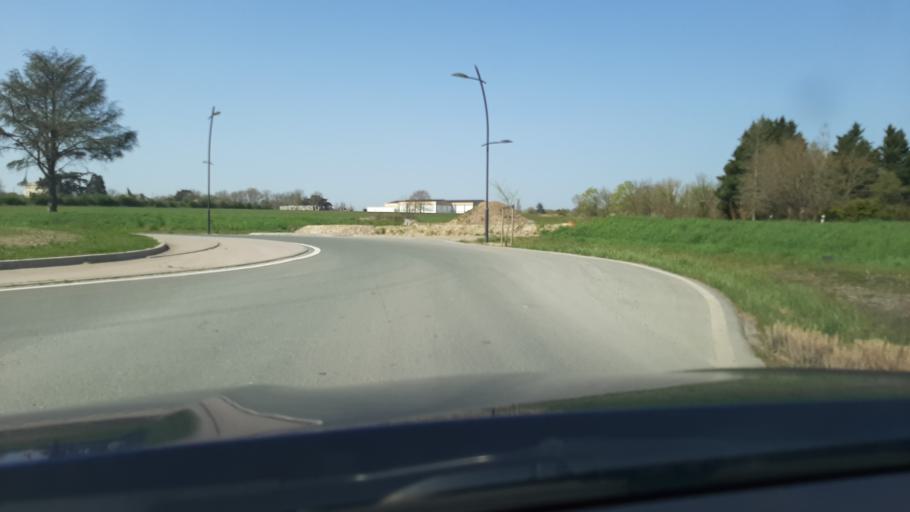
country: FR
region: Pays de la Loire
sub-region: Departement de Maine-et-Loire
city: Pellouailles-les-Vignes
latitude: 47.5143
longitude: -0.4483
